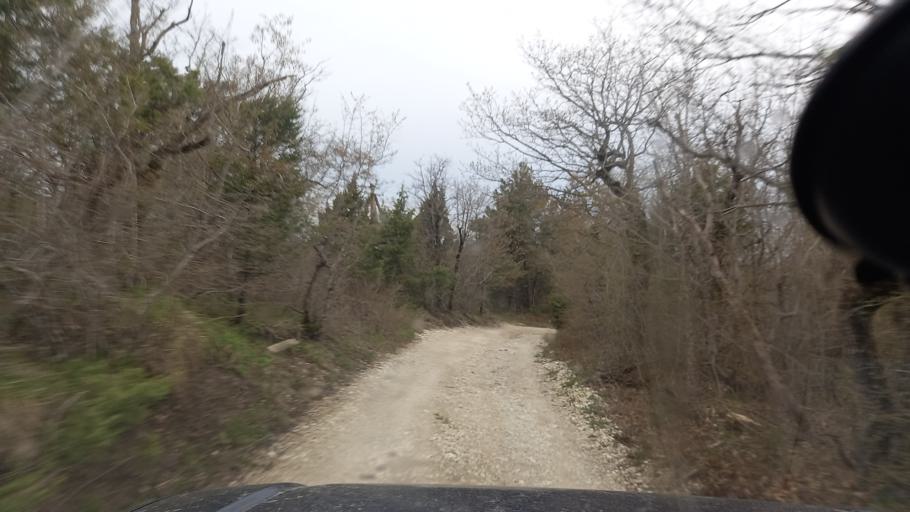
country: RU
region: Krasnodarskiy
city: Dzhubga
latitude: 44.3196
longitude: 38.6735
